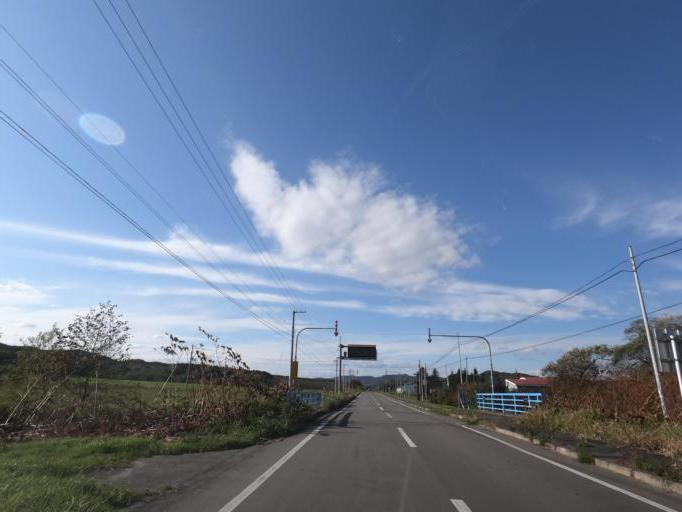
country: JP
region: Hokkaido
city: Obihiro
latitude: 42.5994
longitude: 143.4509
